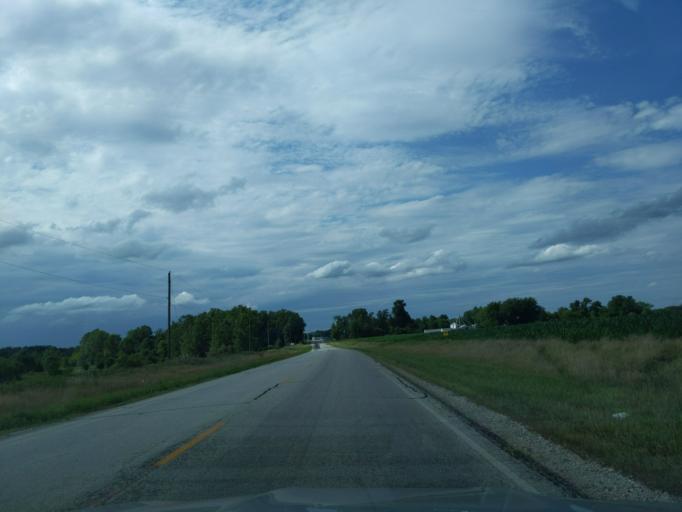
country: US
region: Indiana
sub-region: Ripley County
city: Sunman
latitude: 39.2750
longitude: -85.0981
